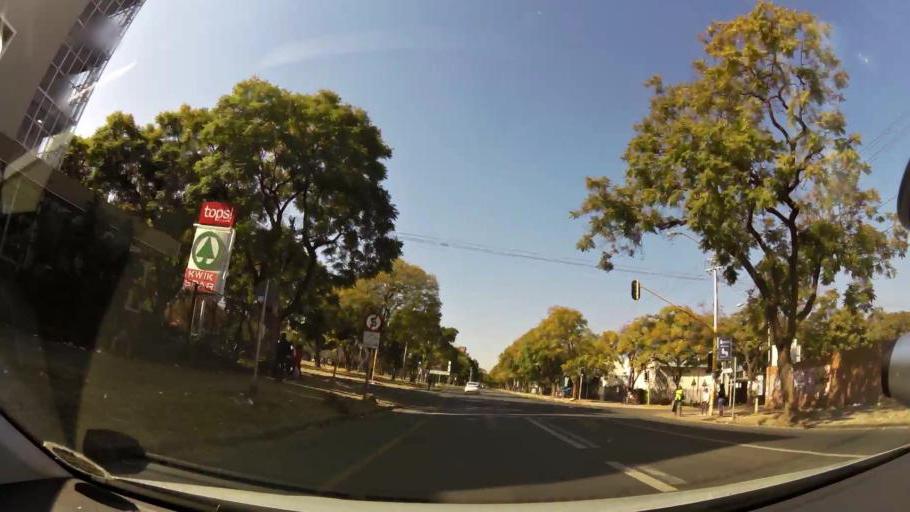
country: ZA
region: Gauteng
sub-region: City of Tshwane Metropolitan Municipality
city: Pretoria
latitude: -25.7494
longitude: 28.2122
